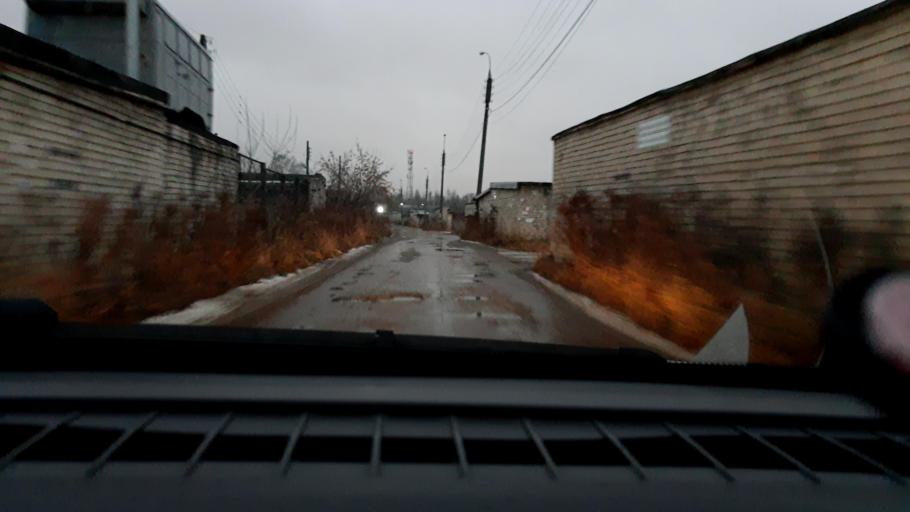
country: RU
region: Nizjnij Novgorod
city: Gorbatovka
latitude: 56.2541
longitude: 43.8377
